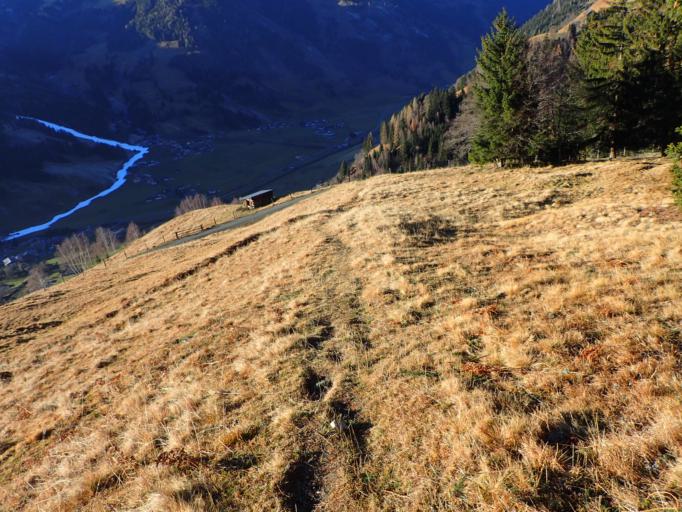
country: AT
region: Salzburg
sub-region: Politischer Bezirk Zell am See
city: Rauris
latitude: 47.2330
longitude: 13.0084
